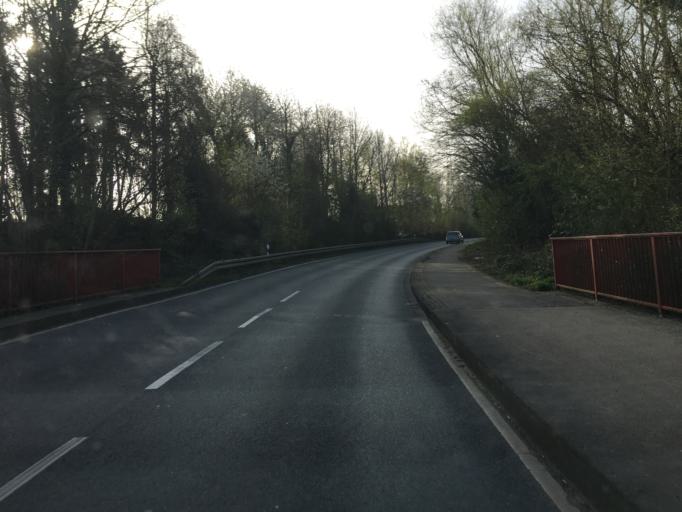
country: DE
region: North Rhine-Westphalia
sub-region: Regierungsbezirk Koln
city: Hurth
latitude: 50.8632
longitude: 6.8570
